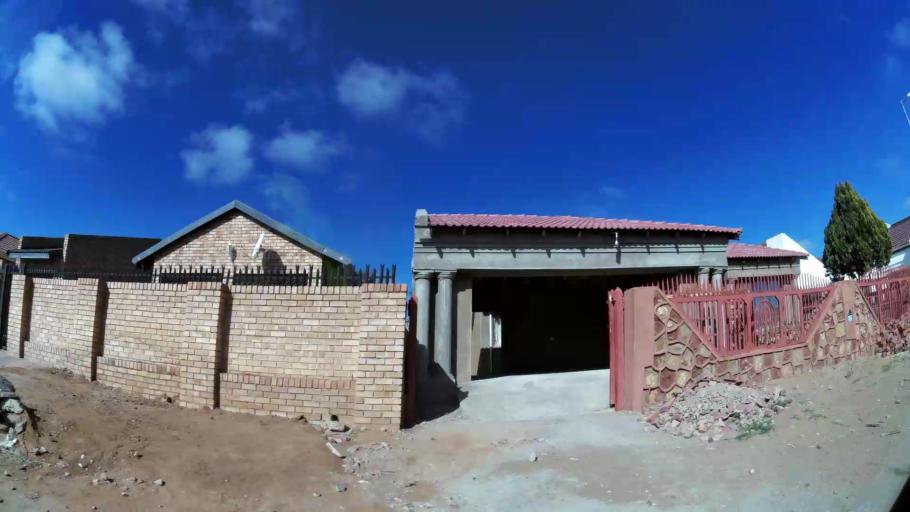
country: ZA
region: Limpopo
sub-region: Capricorn District Municipality
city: Polokwane
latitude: -23.8547
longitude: 29.3736
